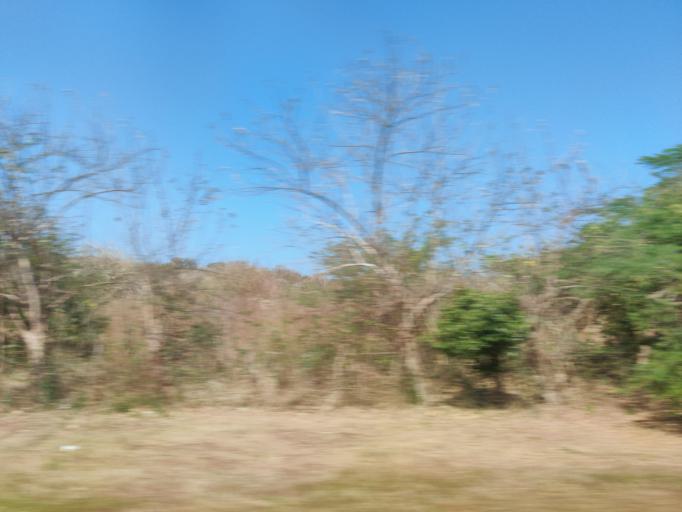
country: CO
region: Atlantico
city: Piojo
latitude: 10.7458
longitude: -75.2521
